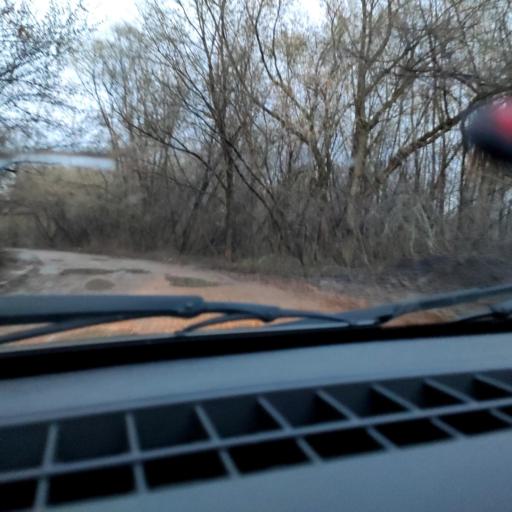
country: RU
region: Bashkortostan
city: Ufa
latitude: 54.6753
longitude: 55.9699
